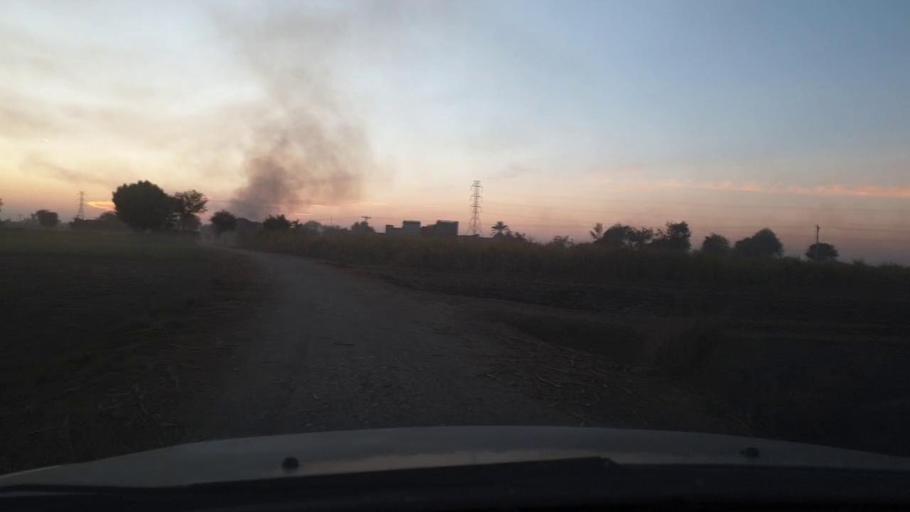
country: PK
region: Sindh
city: Ghotki
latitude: 27.9846
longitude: 69.2670
